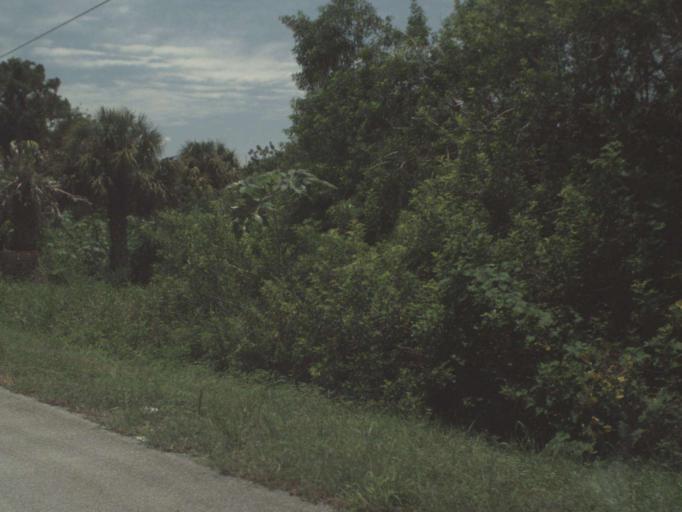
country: US
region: Florida
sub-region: Martin County
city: Indiantown
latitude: 27.0521
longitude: -80.6438
